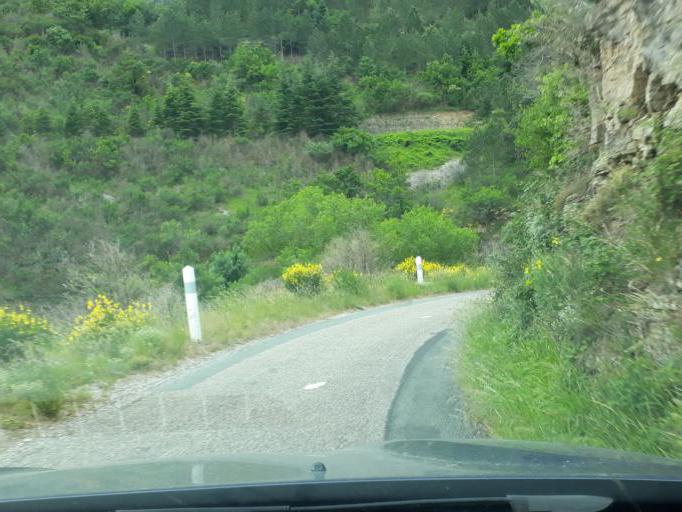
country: FR
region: Languedoc-Roussillon
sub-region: Departement de l'Herault
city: Lodeve
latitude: 43.7914
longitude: 3.2730
